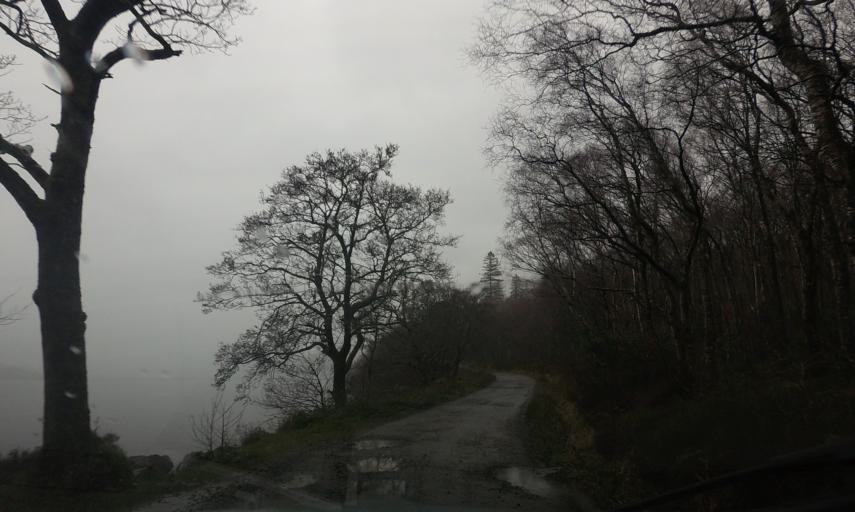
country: GB
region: Scotland
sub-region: West Dunbartonshire
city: Balloch
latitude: 56.1537
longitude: -4.6423
